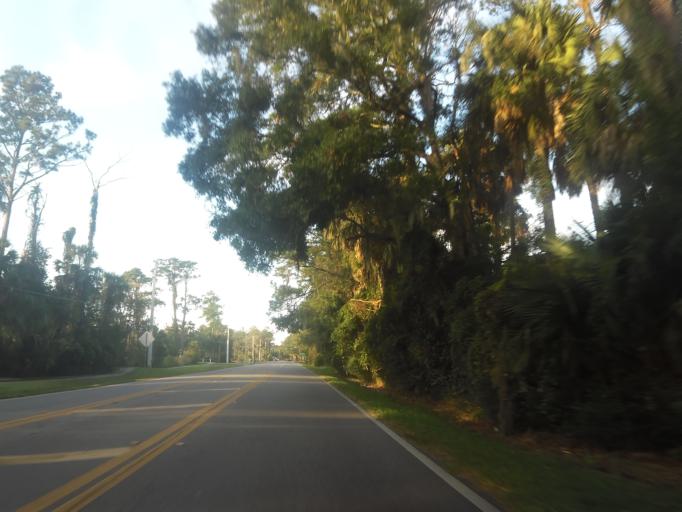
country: US
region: Florida
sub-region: Saint Johns County
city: Palm Valley
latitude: 30.1625
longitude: -81.3858
